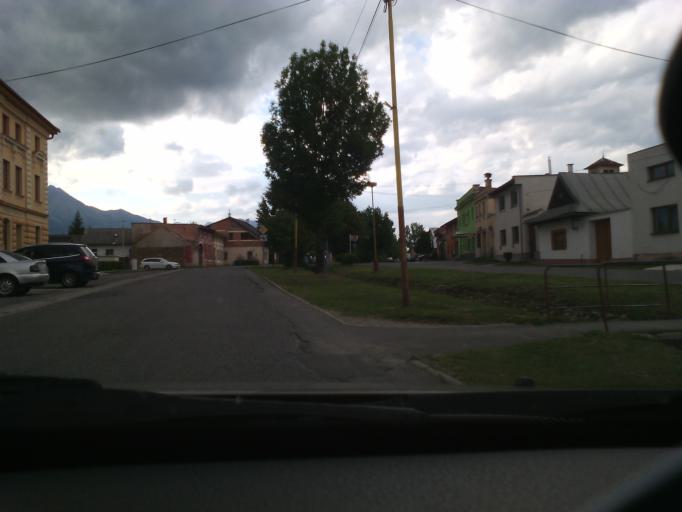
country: SK
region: Presovsky
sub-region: Okres Presov
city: Kezmarok
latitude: 49.1134
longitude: 20.3600
